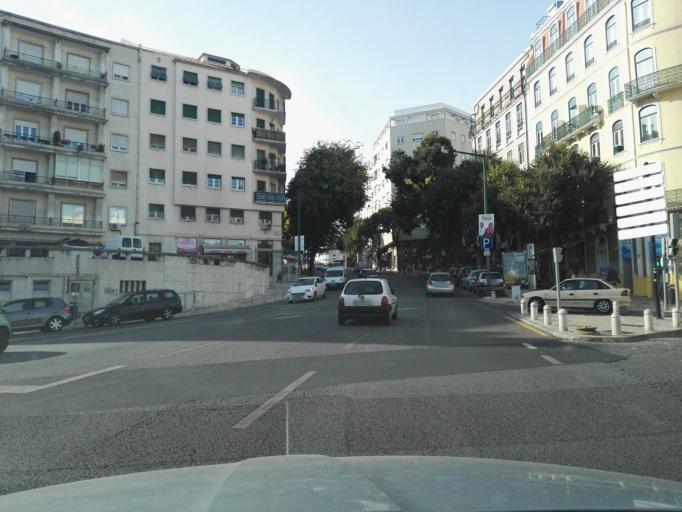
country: PT
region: Lisbon
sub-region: Lisbon
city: Lisbon
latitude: 38.7265
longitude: -9.1363
